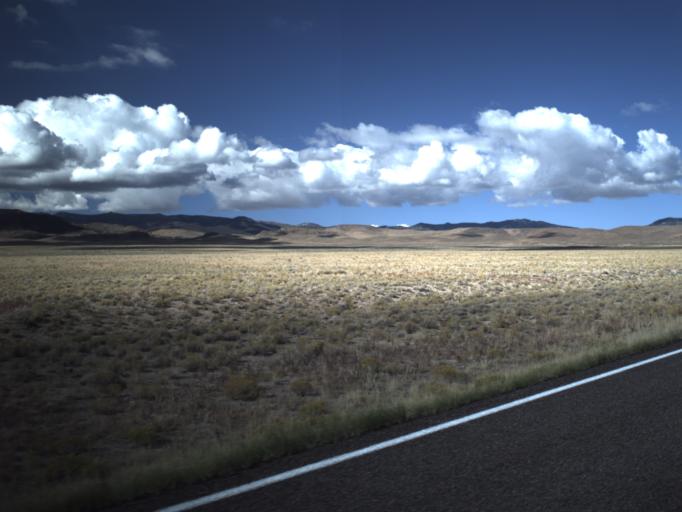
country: US
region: Utah
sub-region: Beaver County
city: Milford
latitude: 38.5739
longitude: -113.7944
